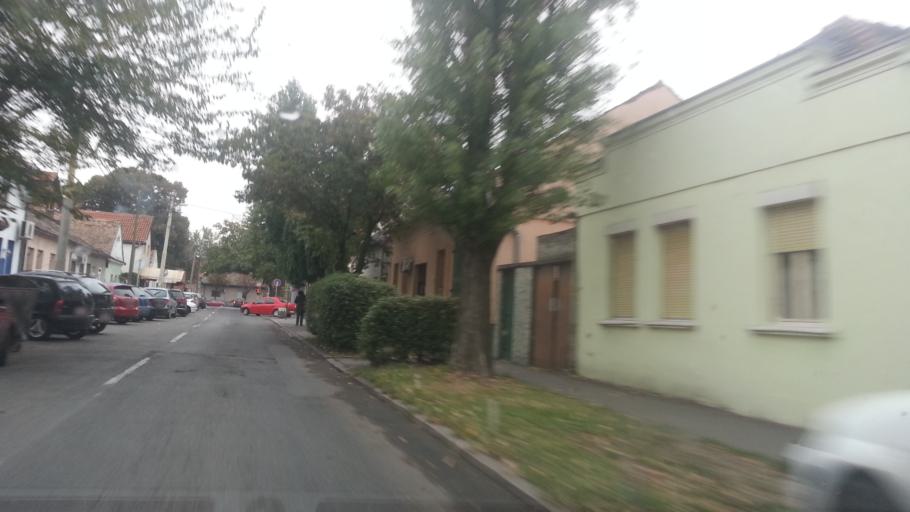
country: RS
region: Central Serbia
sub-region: Belgrade
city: Zemun
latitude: 44.8478
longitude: 20.4028
